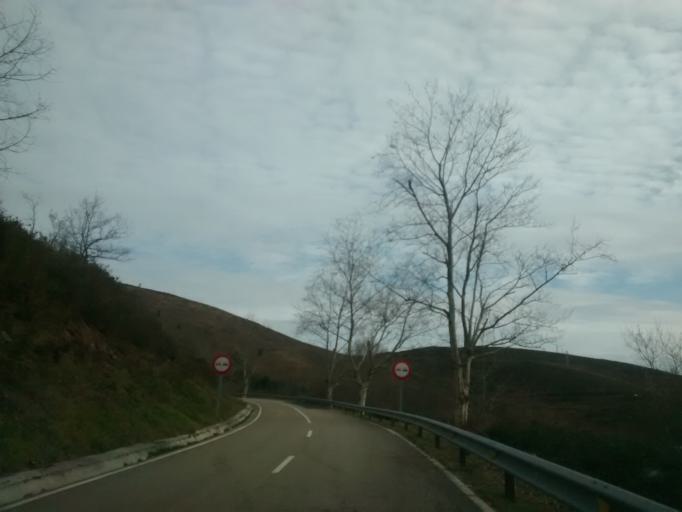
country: ES
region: Cantabria
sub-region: Provincia de Cantabria
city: Ruente
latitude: 43.2475
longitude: -4.3286
